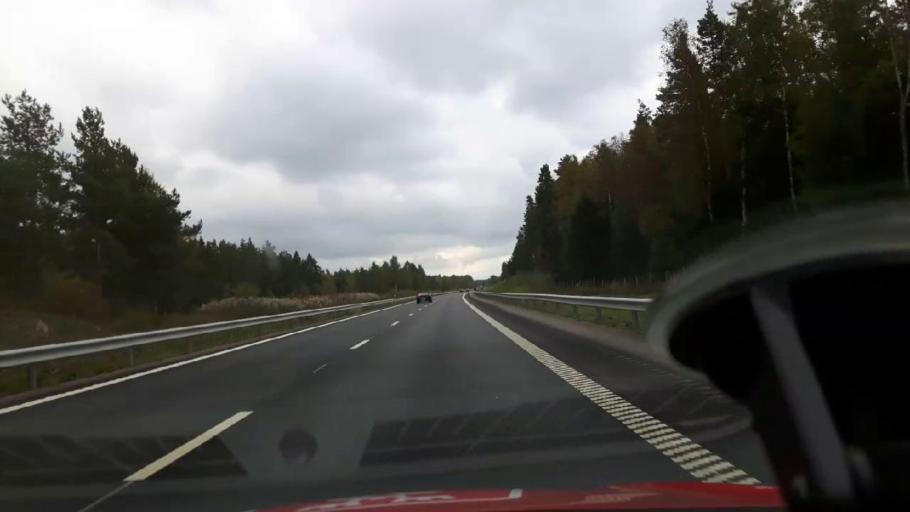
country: SE
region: Gaevleborg
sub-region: Gavle Kommun
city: Gavle
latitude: 60.6056
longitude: 17.1791
